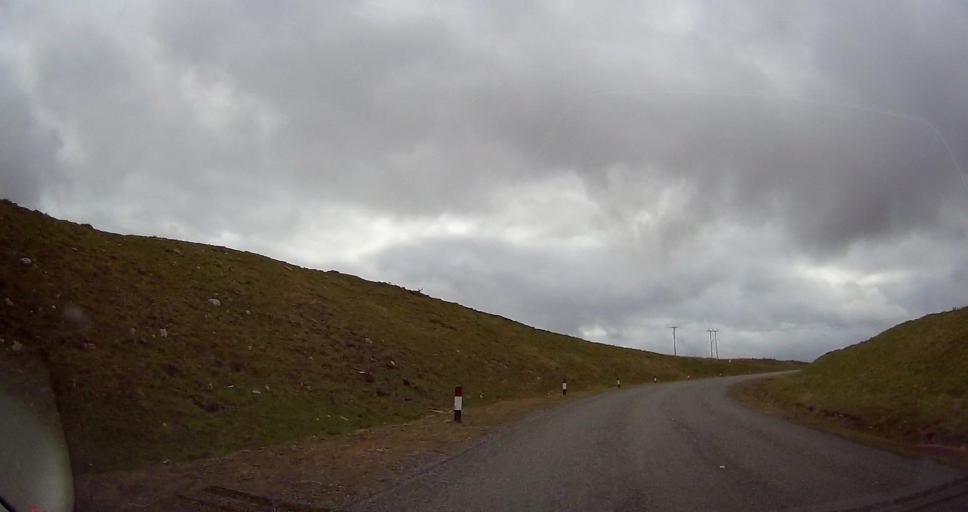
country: GB
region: Scotland
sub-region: Shetland Islands
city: Shetland
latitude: 60.6697
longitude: -1.0647
